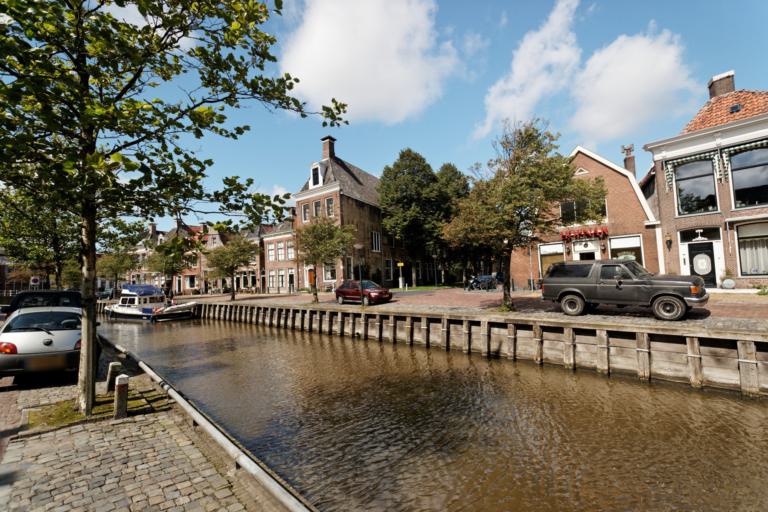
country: NL
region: Friesland
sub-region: Gemeente Harlingen
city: Harlingen
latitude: 53.1743
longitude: 5.4229
